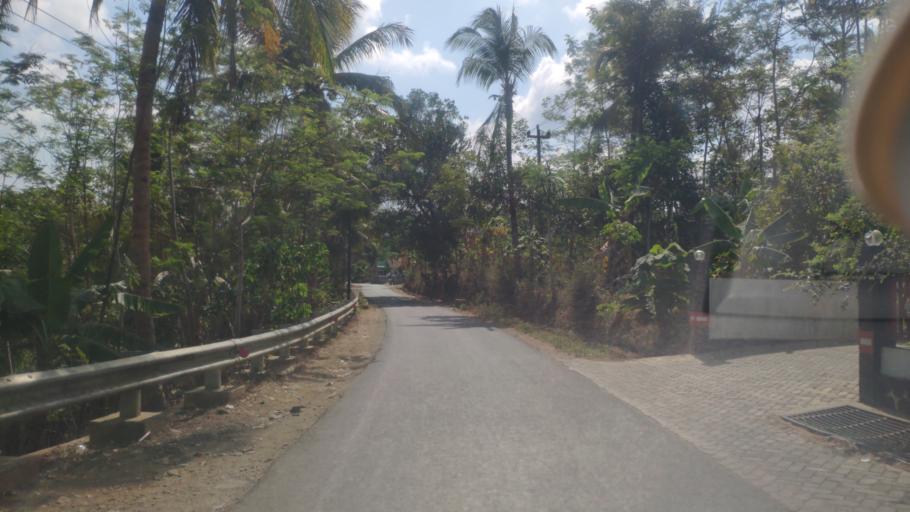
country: ID
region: Central Java
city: Gombong
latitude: -7.4227
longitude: 109.6602
